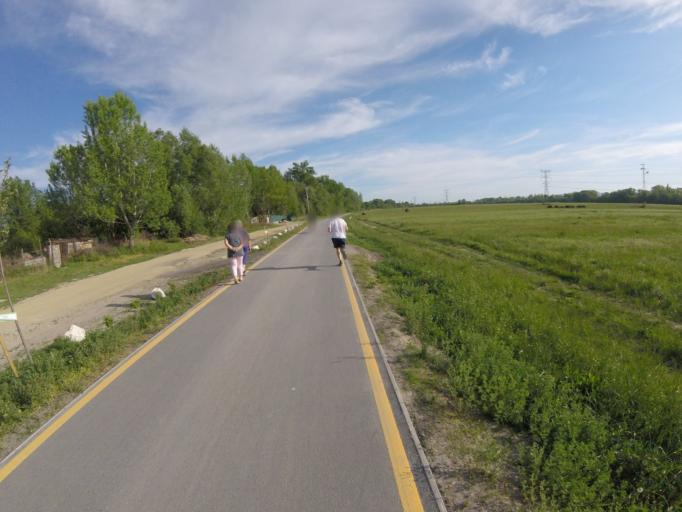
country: HU
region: Pest
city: Dunakeszi
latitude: 47.6382
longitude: 19.1227
